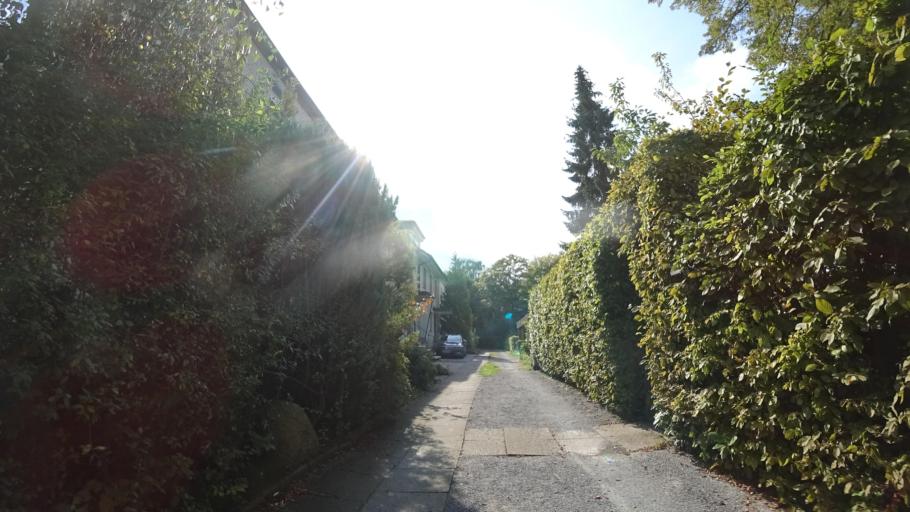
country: DE
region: North Rhine-Westphalia
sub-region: Regierungsbezirk Detmold
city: Bielefeld
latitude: 52.0453
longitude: 8.5356
